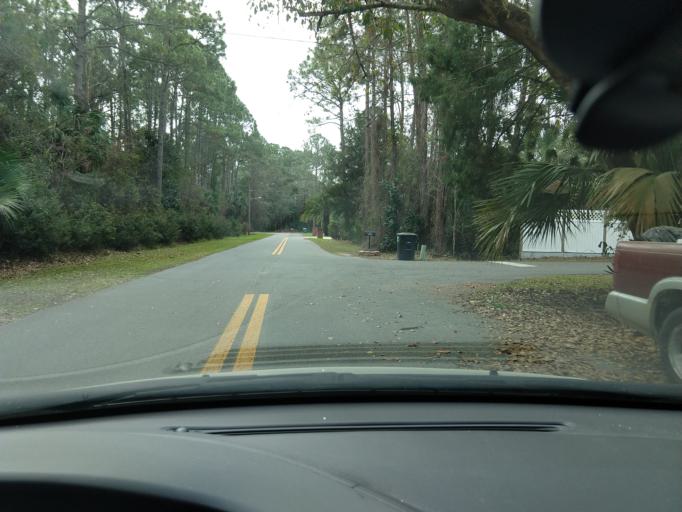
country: US
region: Florida
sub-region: Franklin County
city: Apalachicola
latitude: 29.7178
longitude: -85.0310
